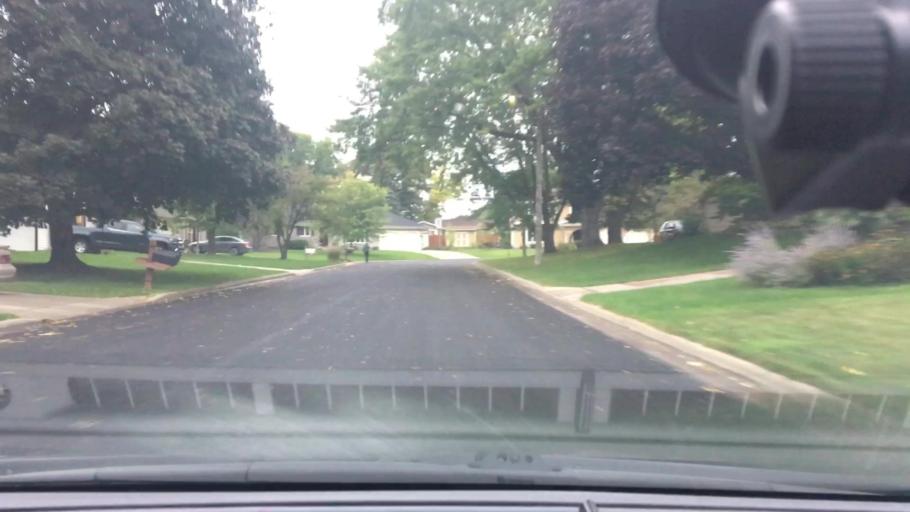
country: US
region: Minnesota
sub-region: Hennepin County
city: New Hope
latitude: 45.0083
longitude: -93.3882
